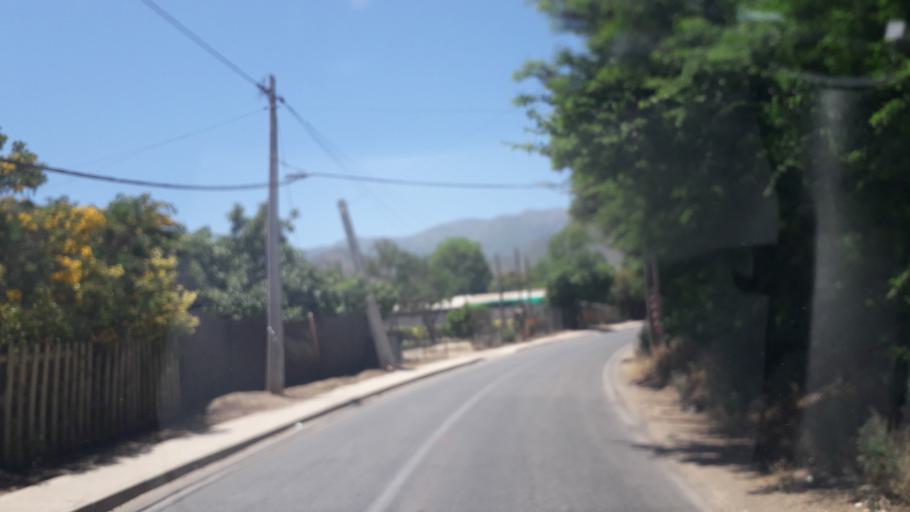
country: CL
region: Valparaiso
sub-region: Provincia de Quillota
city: Quillota
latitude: -32.9077
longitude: -71.2143
